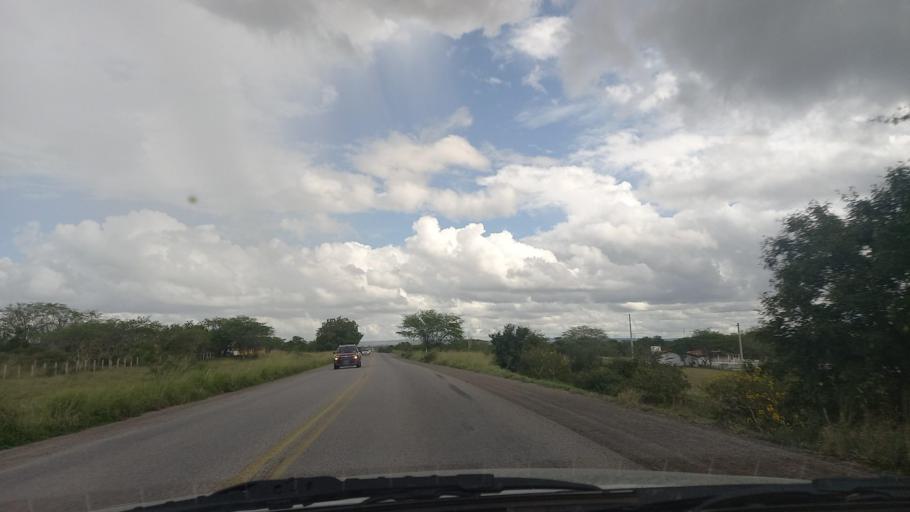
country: BR
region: Pernambuco
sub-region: Cachoeirinha
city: Cachoeirinha
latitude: -8.5373
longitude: -36.2672
